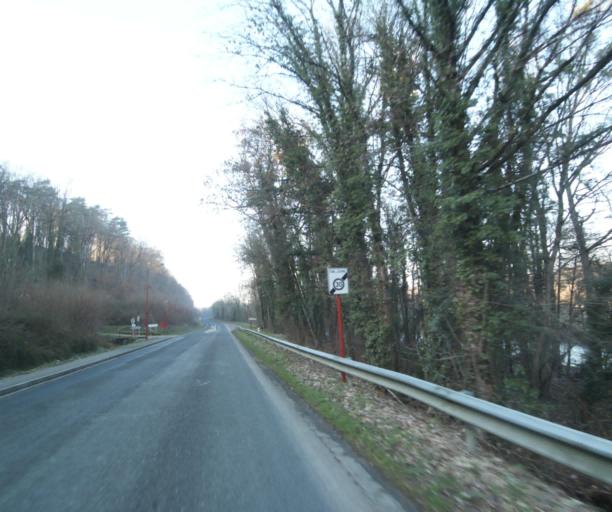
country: FR
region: Champagne-Ardenne
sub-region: Departement de la Haute-Marne
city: Bienville
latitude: 48.5506
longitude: 5.0705
